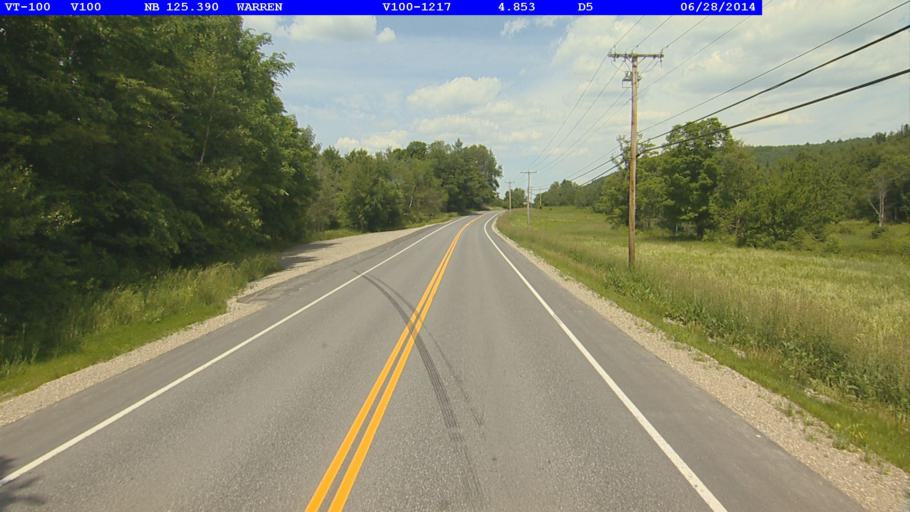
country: US
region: Vermont
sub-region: Washington County
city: Northfield
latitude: 44.1269
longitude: -72.8514
